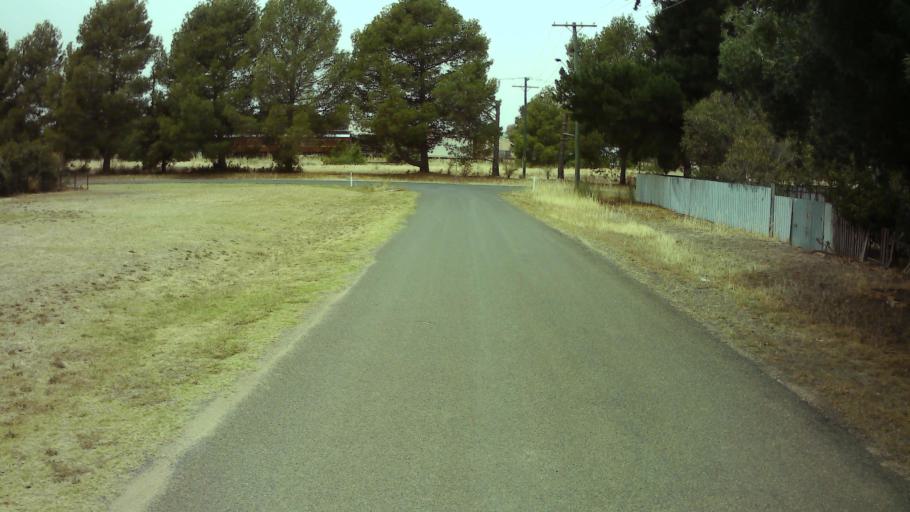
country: AU
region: New South Wales
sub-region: Weddin
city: Grenfell
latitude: -33.8966
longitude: 148.1538
